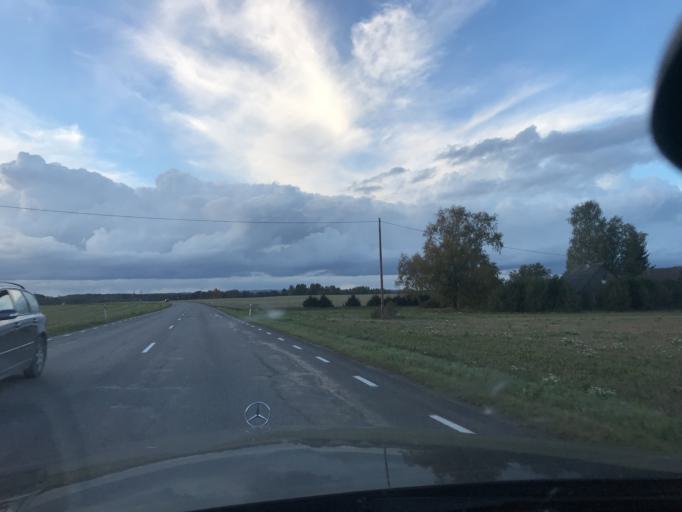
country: EE
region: Vorumaa
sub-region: Antsla vald
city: Vana-Antsla
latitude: 57.8991
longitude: 26.4800
